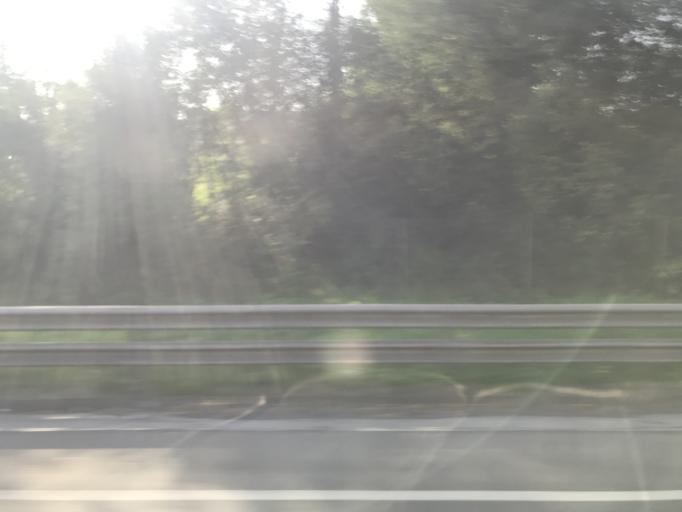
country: ES
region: Basque Country
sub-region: Provincia de Guipuzcoa
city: Beasain
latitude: 43.0405
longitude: -2.2157
